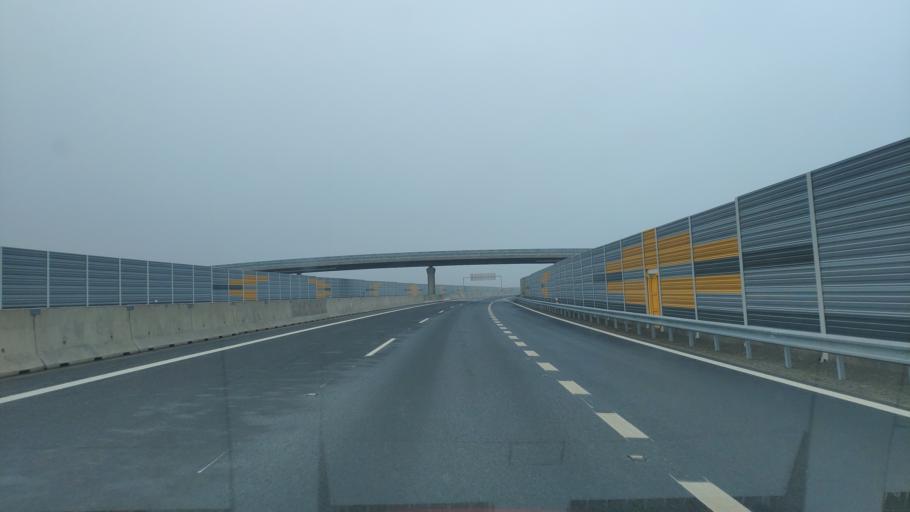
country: SK
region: Kosicky
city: Kosice
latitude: 48.7486
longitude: 21.3324
